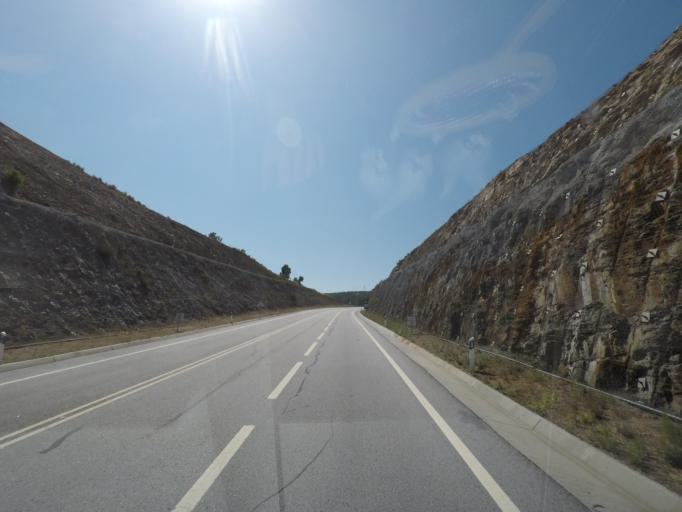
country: PT
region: Braganca
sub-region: Braganca Municipality
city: Vila Flor
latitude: 41.3129
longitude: -7.1244
